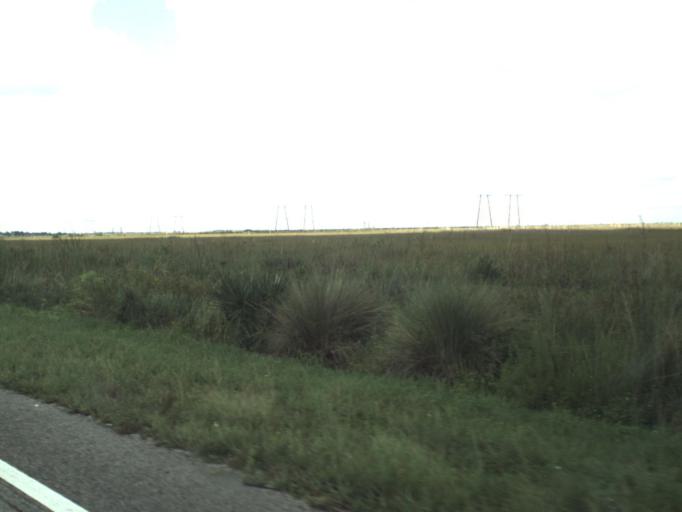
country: US
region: Florida
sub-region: Miami-Dade County
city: Palm Springs North
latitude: 25.9647
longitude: -80.4316
